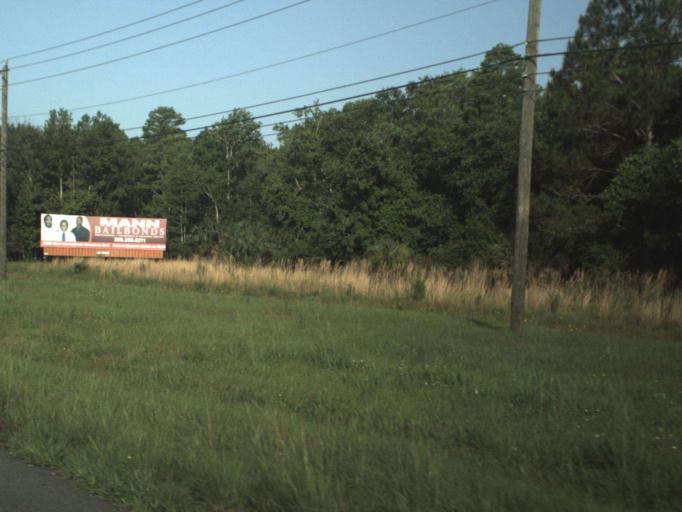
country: US
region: Florida
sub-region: Volusia County
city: Daytona Beach
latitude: 29.1507
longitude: -81.1097
